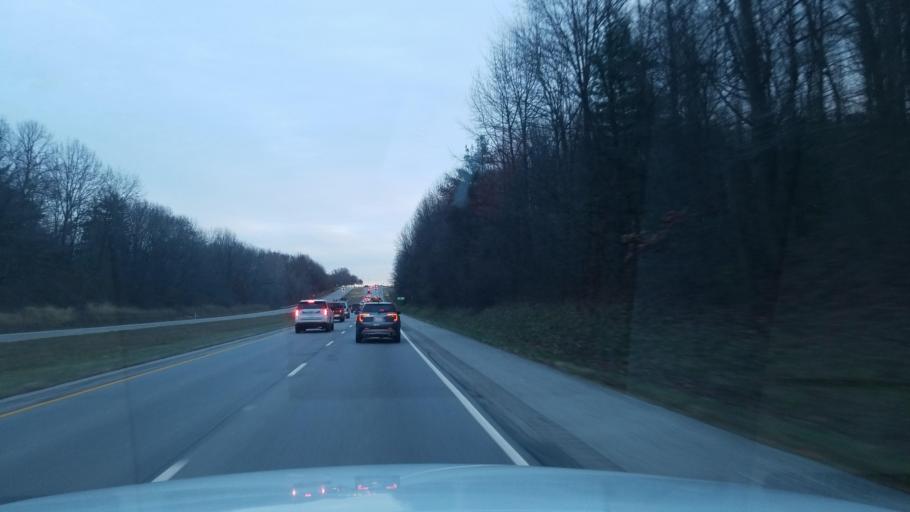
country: US
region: Indiana
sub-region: Vanderburgh County
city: Evansville
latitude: 37.9726
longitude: -87.6532
